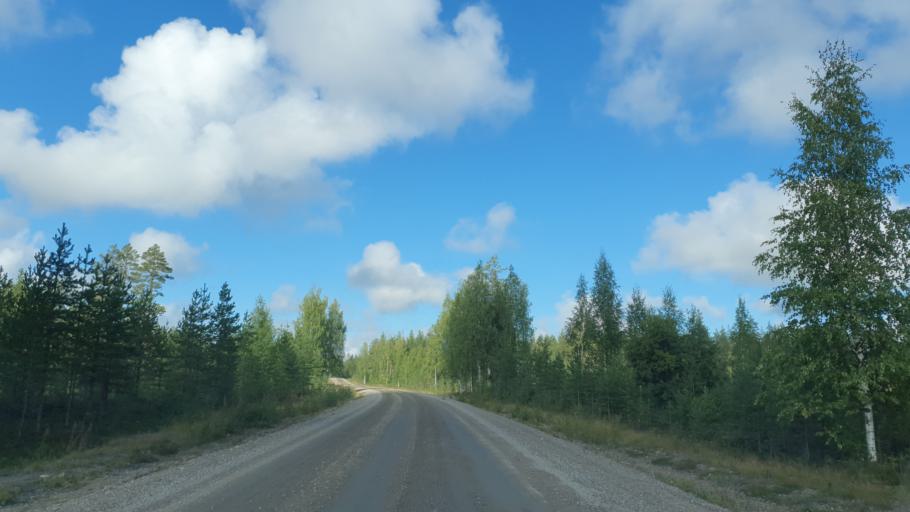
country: FI
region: Kainuu
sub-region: Kehys-Kainuu
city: Kuhmo
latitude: 63.9889
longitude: 29.2197
